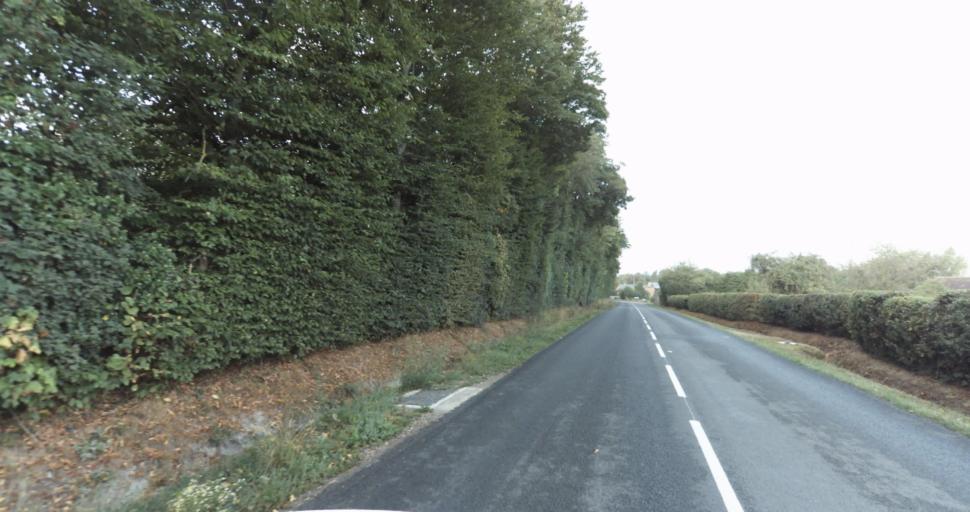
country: FR
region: Lower Normandy
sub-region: Departement de l'Orne
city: Vimoutiers
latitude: 48.9330
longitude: 0.2198
